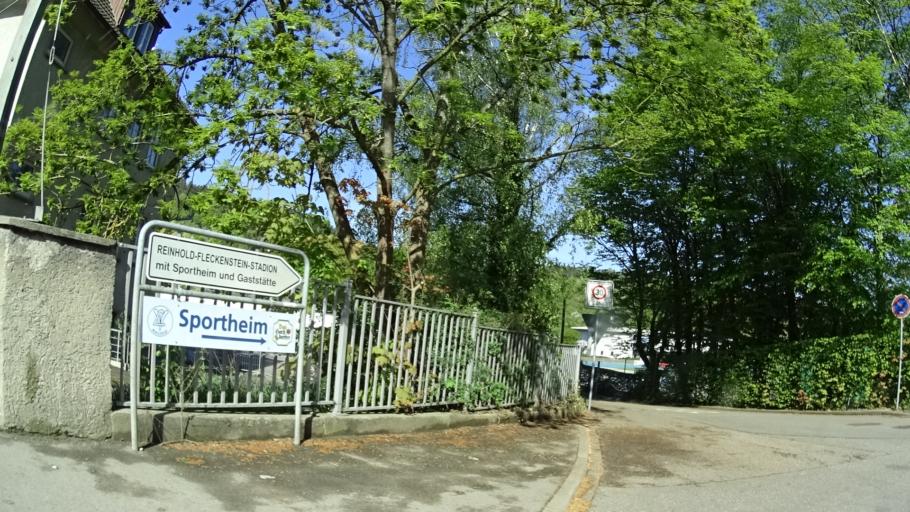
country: DE
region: Baden-Wuerttemberg
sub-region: Karlsruhe Region
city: Nagold
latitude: 48.5592
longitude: 8.7255
